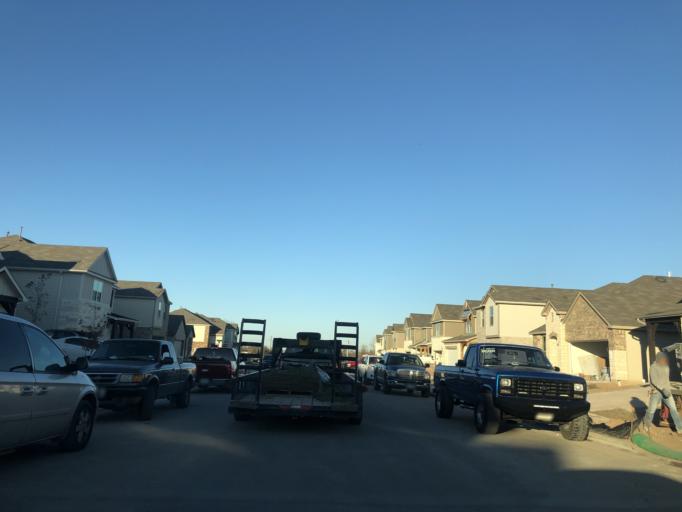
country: US
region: Texas
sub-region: Travis County
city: Wells Branch
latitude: 30.4635
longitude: -97.6765
